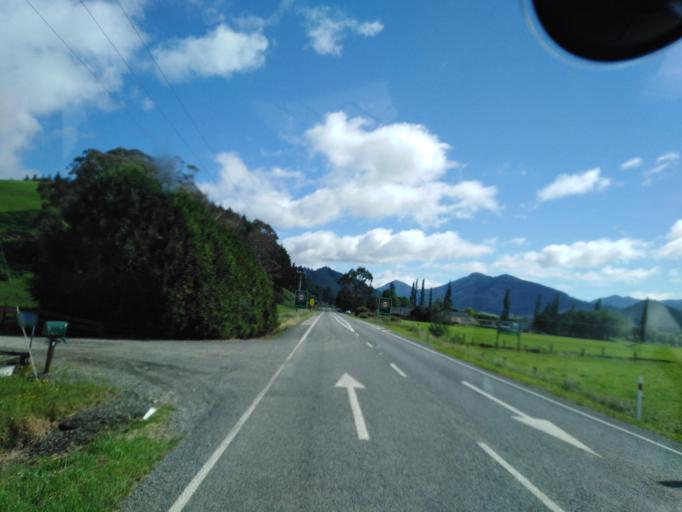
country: NZ
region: Nelson
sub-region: Nelson City
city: Nelson
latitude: -41.2365
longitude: 173.5803
